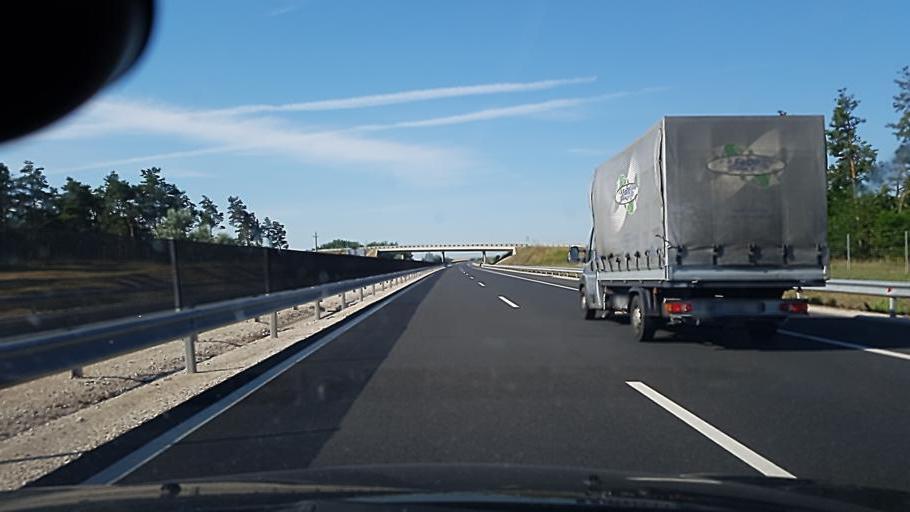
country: HU
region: Tolna
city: Paks
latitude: 46.5913
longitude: 18.8168
